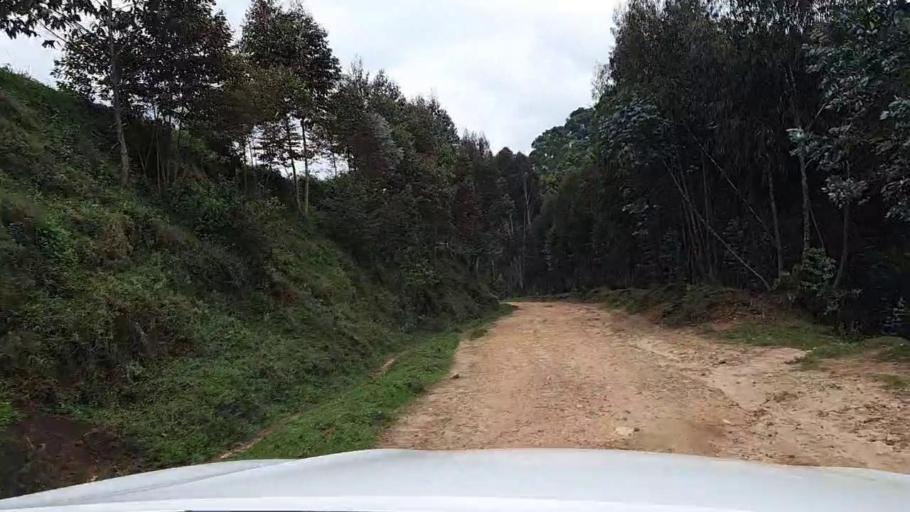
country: RW
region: Western Province
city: Kibuye
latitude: -2.2804
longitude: 29.3682
